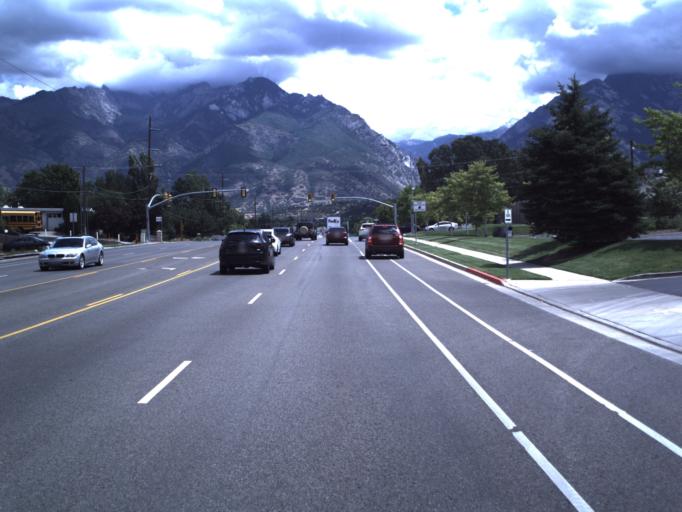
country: US
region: Utah
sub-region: Salt Lake County
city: Sandy Hills
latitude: 40.5803
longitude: -111.8453
